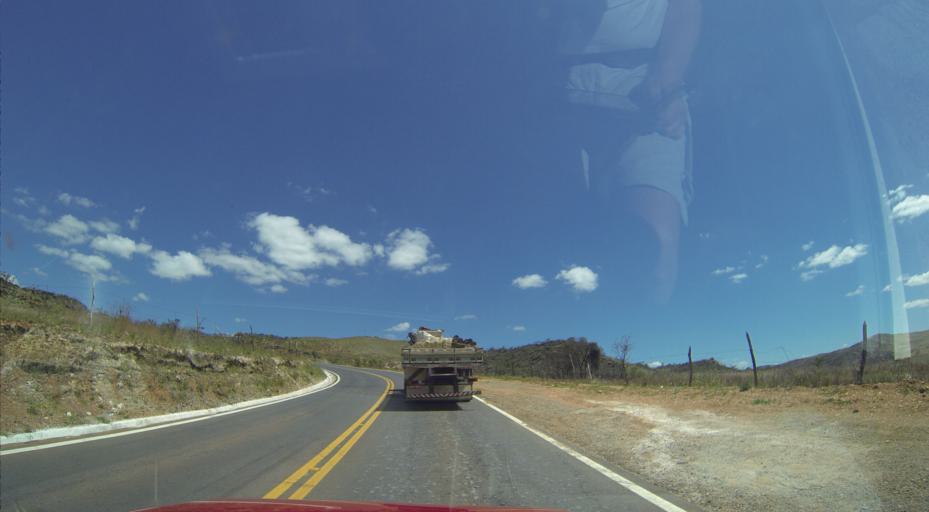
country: BR
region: Minas Gerais
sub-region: Conceicao Do Mato Dentro
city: Conceicao do Mato Dentro
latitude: -19.2851
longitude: -43.5765
